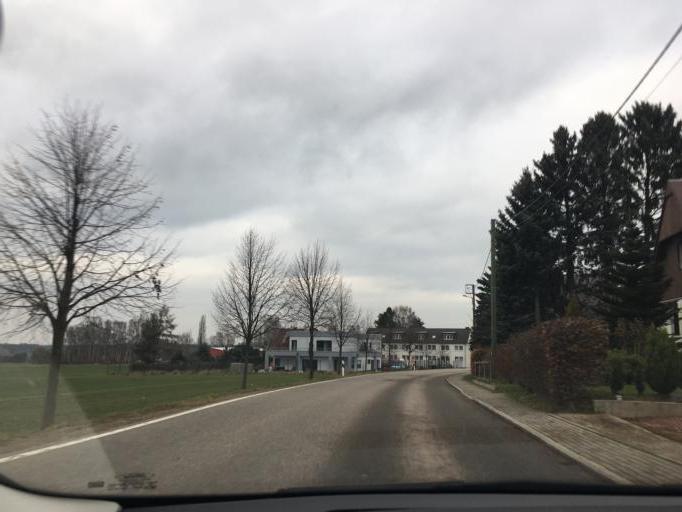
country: DE
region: Saxony
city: Hohenstein-Ernstthal
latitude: 50.8290
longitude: 12.7046
